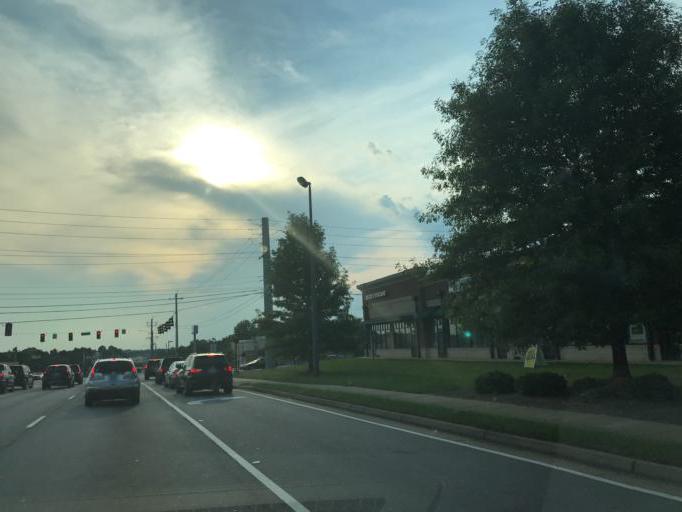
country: US
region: Alabama
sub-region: Russell County
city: Phenix City
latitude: 32.5397
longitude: -84.9534
